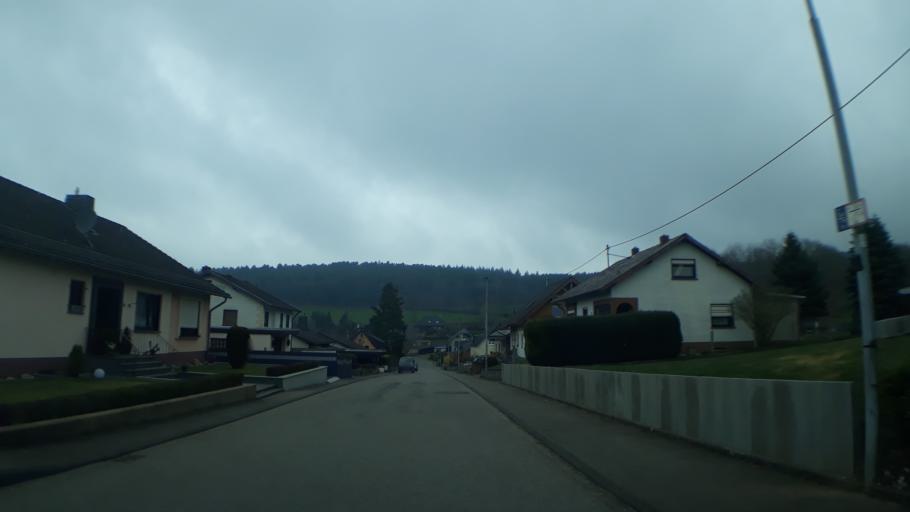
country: DE
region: North Rhine-Westphalia
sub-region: Regierungsbezirk Koln
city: Kall
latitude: 50.5254
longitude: 6.5637
